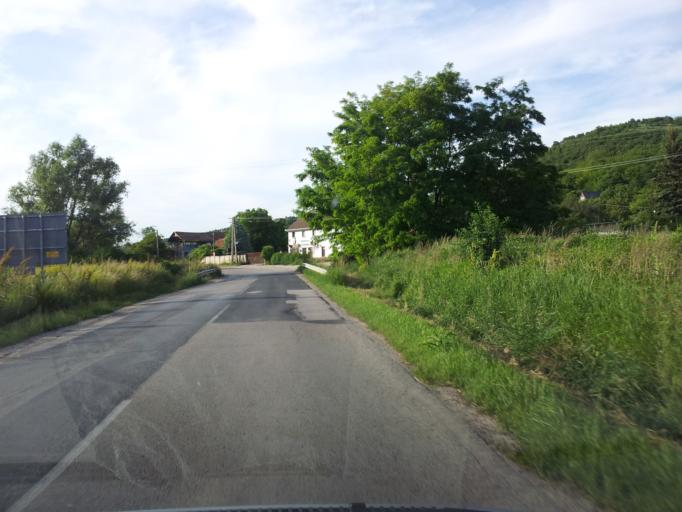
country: HU
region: Komarom-Esztergom
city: Esztergom
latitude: 47.7696
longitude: 18.7577
